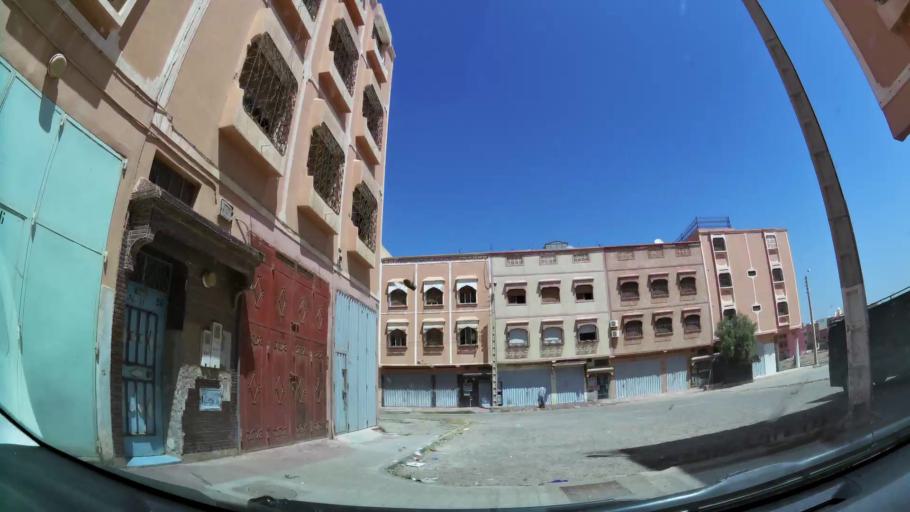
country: MA
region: Souss-Massa-Draa
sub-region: Inezgane-Ait Mellou
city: Inezgane
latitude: 30.3364
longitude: -9.4993
